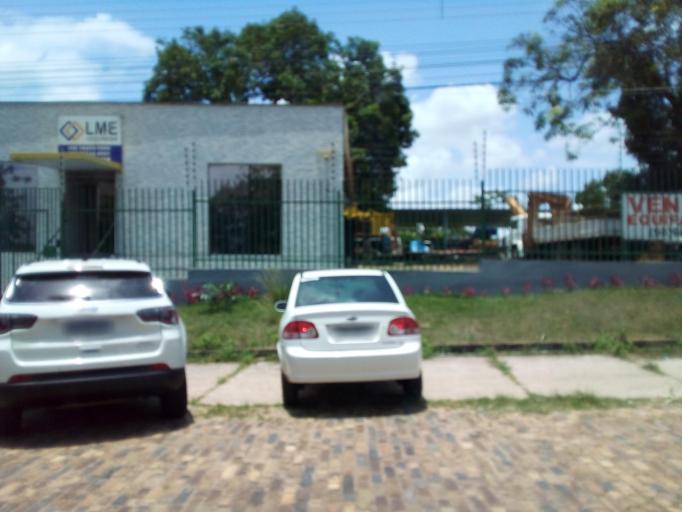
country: BR
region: Maranhao
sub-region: Sao Luis
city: Sao Luis
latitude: -2.6997
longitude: -44.3084
